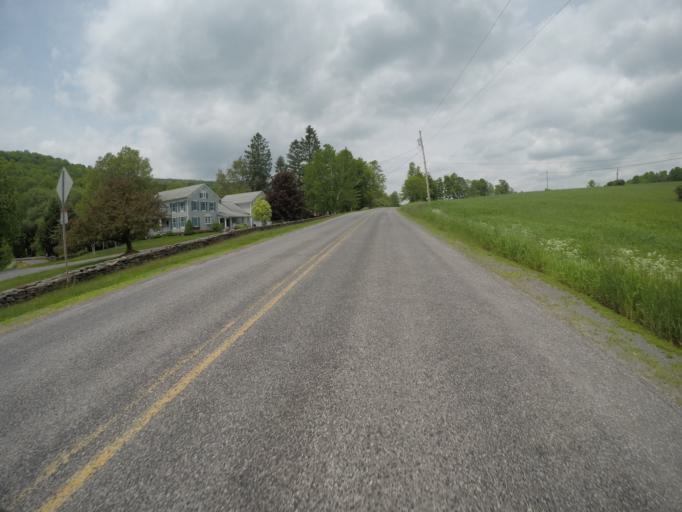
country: US
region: New York
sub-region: Delaware County
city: Stamford
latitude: 42.1960
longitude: -74.6759
